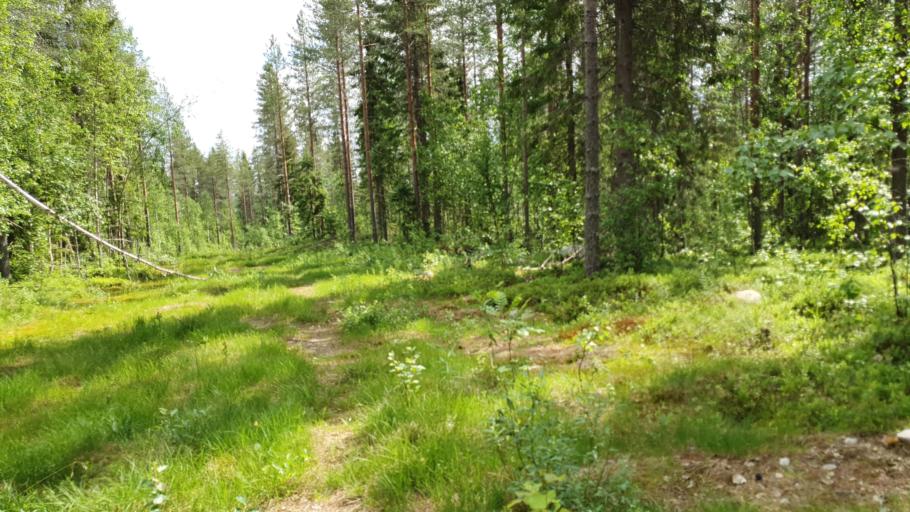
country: FI
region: Kainuu
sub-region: Kehys-Kainuu
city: Kuhmo
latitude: 64.4414
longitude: 29.6922
